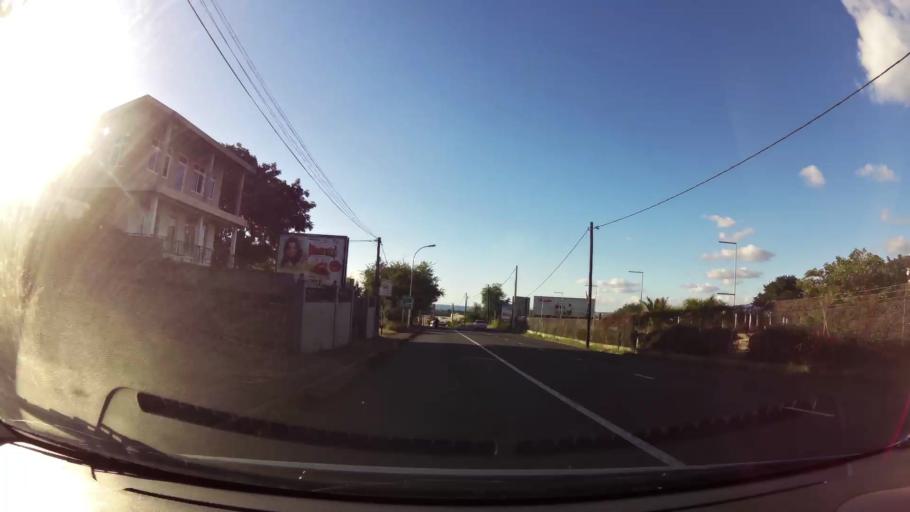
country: MU
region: Moka
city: Pailles
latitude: -20.1846
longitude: 57.4702
